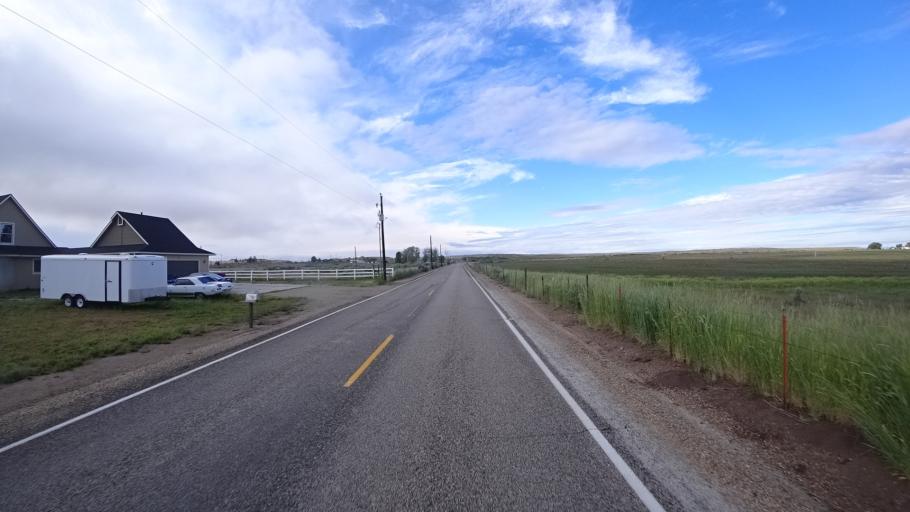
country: US
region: Idaho
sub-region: Ada County
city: Star
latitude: 43.7752
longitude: -116.4731
